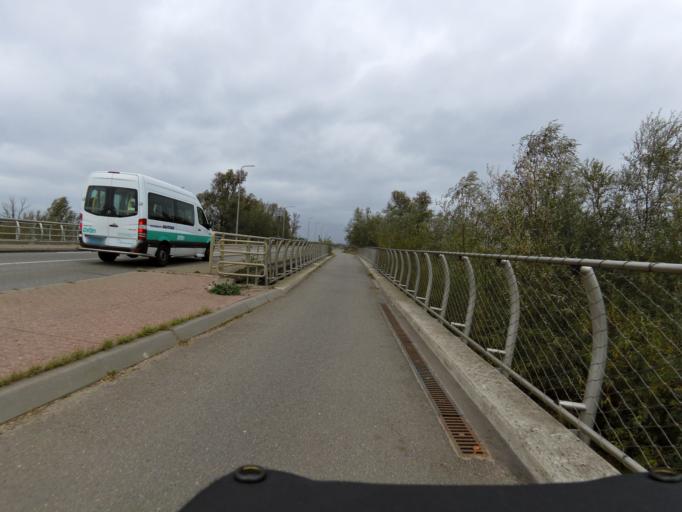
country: NL
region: Gelderland
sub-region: Gemeente Zevenaar
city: Zevenaar
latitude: 51.8912
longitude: 6.1022
